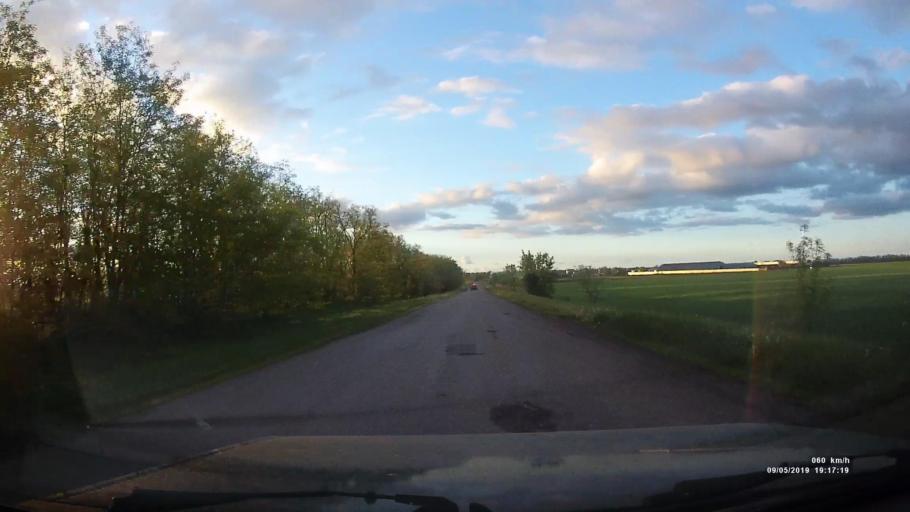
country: RU
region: Krasnodarskiy
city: Kanelovskaya
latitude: 46.7845
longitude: 39.2117
